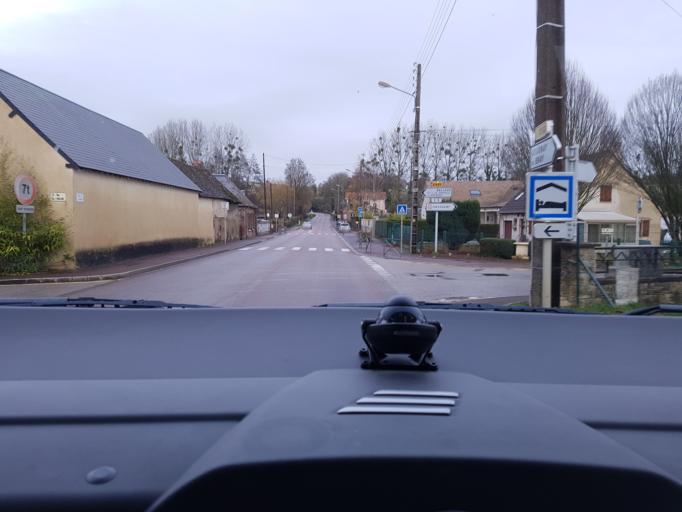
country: FR
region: Picardie
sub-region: Departement de l'Oise
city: Songeons
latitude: 49.5354
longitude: 1.8691
